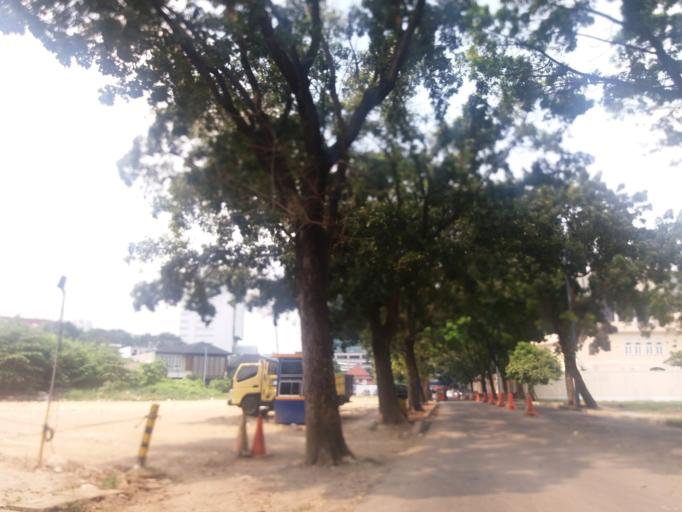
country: ID
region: Jakarta Raya
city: Jakarta
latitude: -6.2306
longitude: 106.8291
